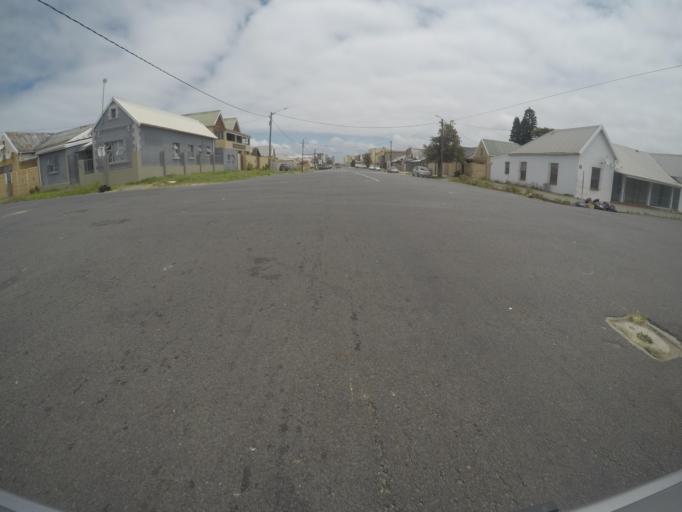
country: ZA
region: Eastern Cape
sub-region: Buffalo City Metropolitan Municipality
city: East London
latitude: -33.0134
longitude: 27.9138
